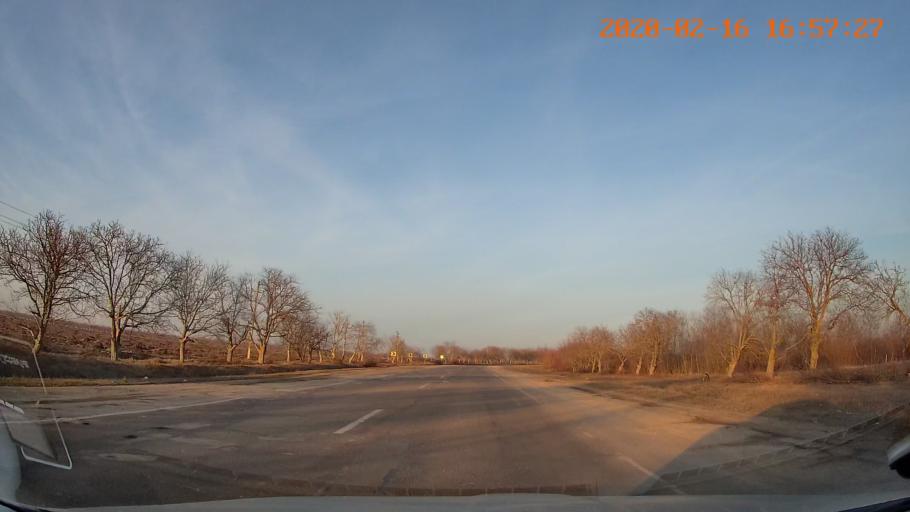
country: MD
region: Briceni
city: Briceni
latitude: 48.3424
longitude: 27.0685
